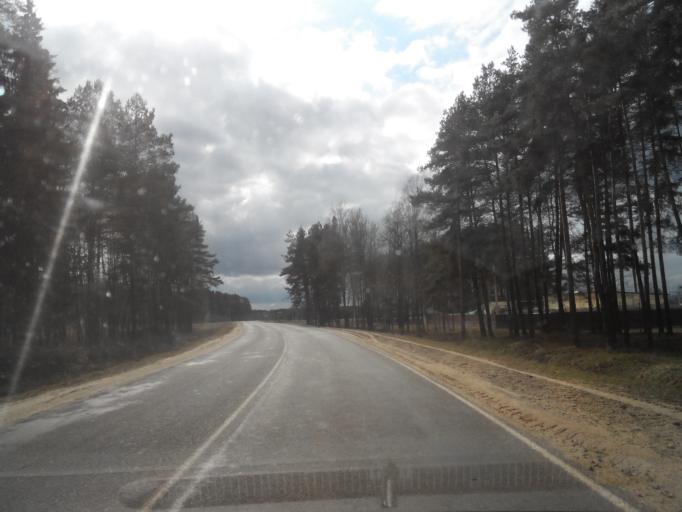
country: BY
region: Vitebsk
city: Pastavy
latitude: 55.1015
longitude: 26.8603
